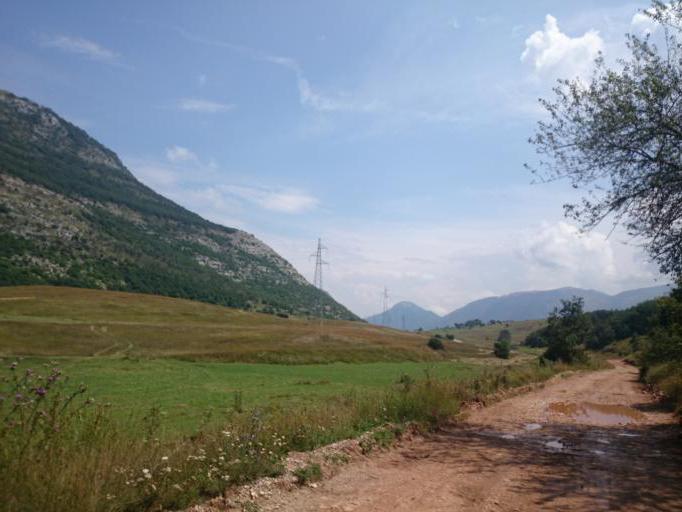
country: AL
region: Diber
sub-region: Rrethi i Dibres
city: Fushe-Lure
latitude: 41.8336
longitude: 20.1640
